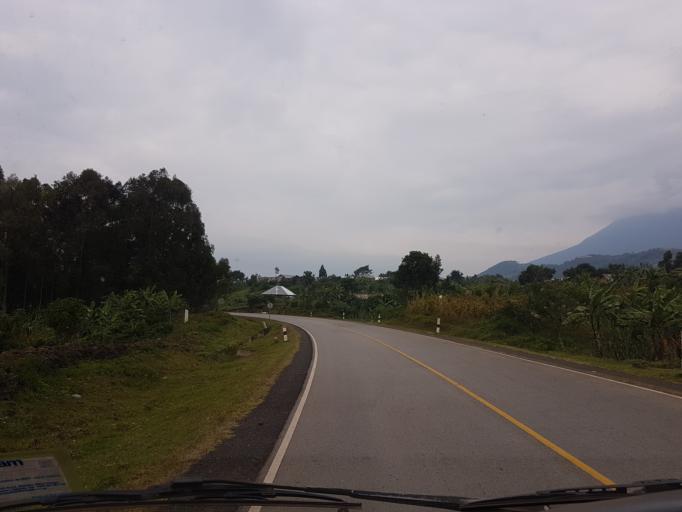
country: UG
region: Western Region
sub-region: Kisoro District
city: Kisoro
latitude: -1.3275
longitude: 29.7286
